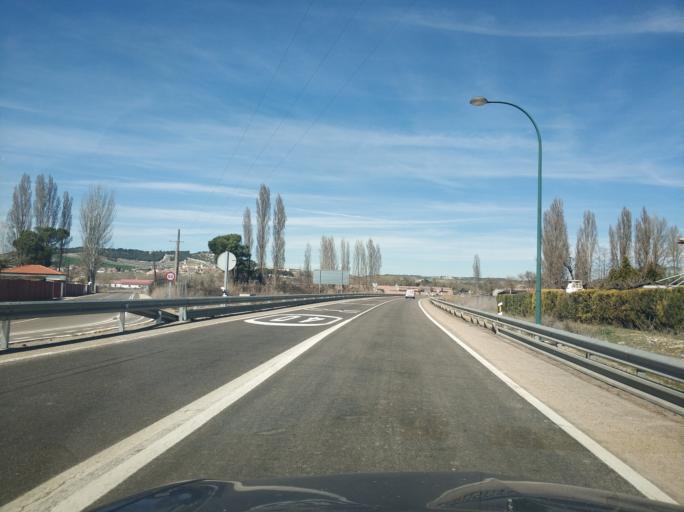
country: ES
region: Castille and Leon
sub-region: Provincia de Valladolid
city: Simancas
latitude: 41.5818
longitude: -4.8154
